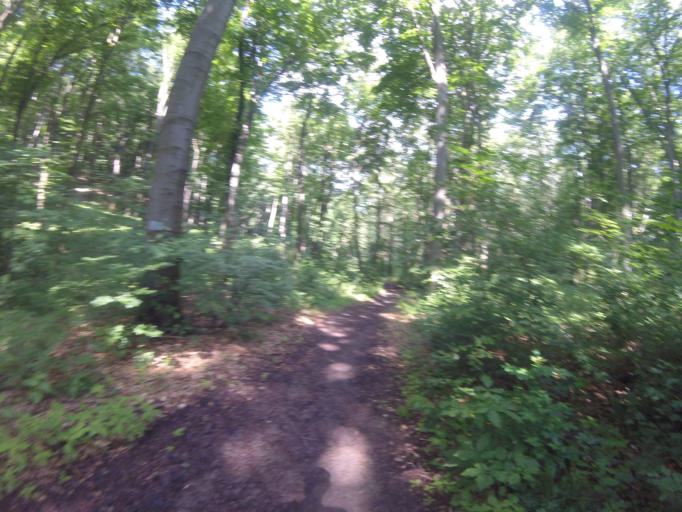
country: HU
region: Veszprem
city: Cseteny
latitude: 47.2782
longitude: 18.0307
